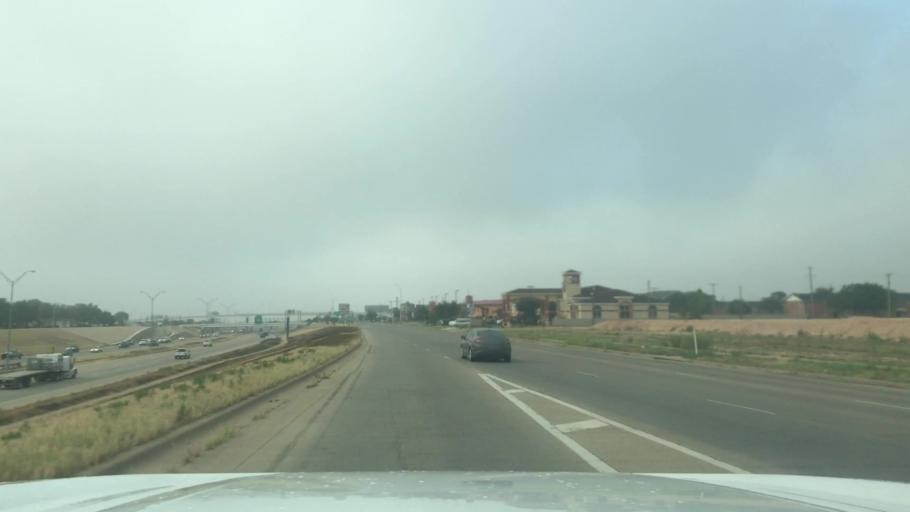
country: US
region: Texas
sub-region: Lubbock County
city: Lubbock
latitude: 33.5449
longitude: -101.8456
